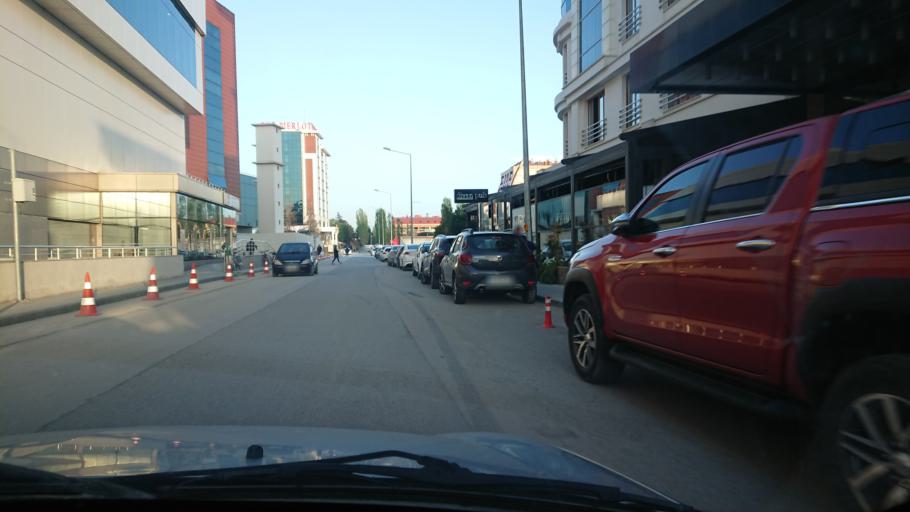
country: TR
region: Eskisehir
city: Eskisehir
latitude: 39.7839
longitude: 30.4969
